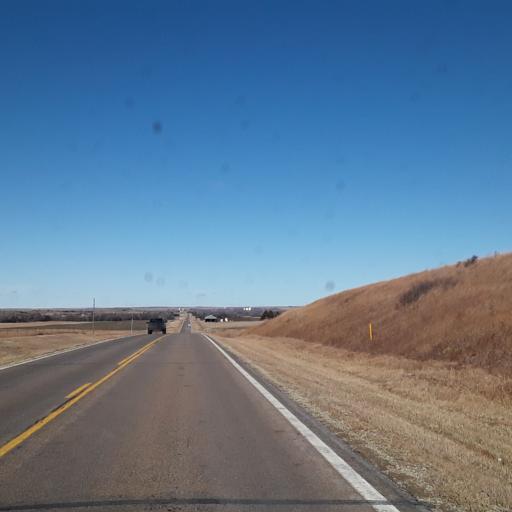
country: US
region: Kansas
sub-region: Lincoln County
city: Lincoln
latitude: 38.9595
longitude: -98.1512
